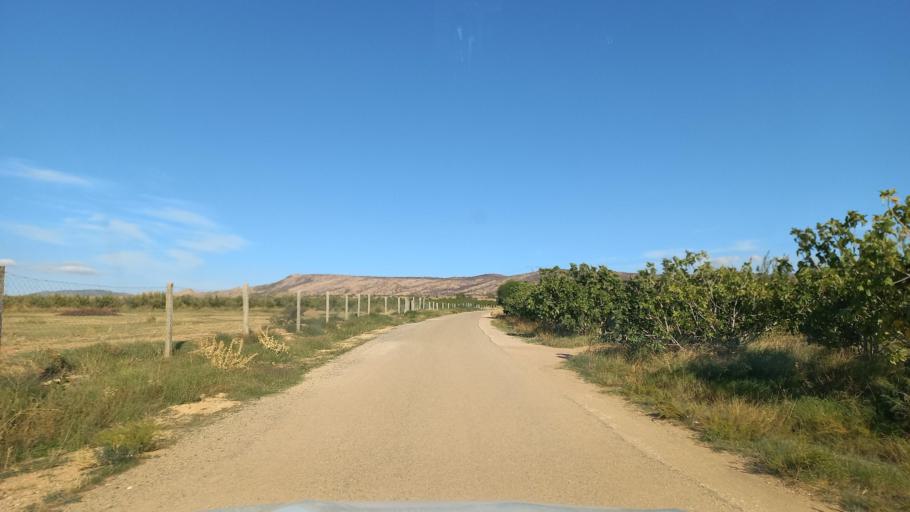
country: TN
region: Al Qasrayn
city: Sbiba
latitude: 35.3351
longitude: 9.1195
